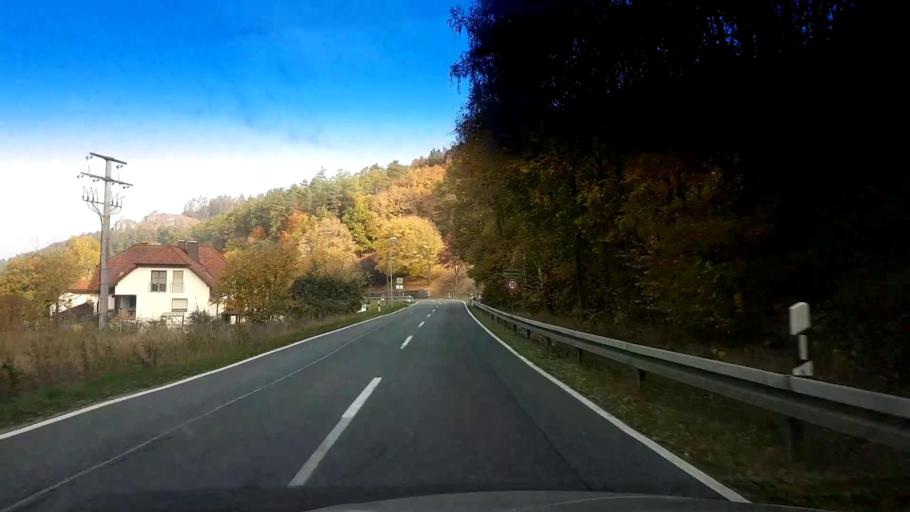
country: DE
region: Bavaria
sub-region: Upper Franconia
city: Weismain
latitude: 50.0500
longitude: 11.2300
